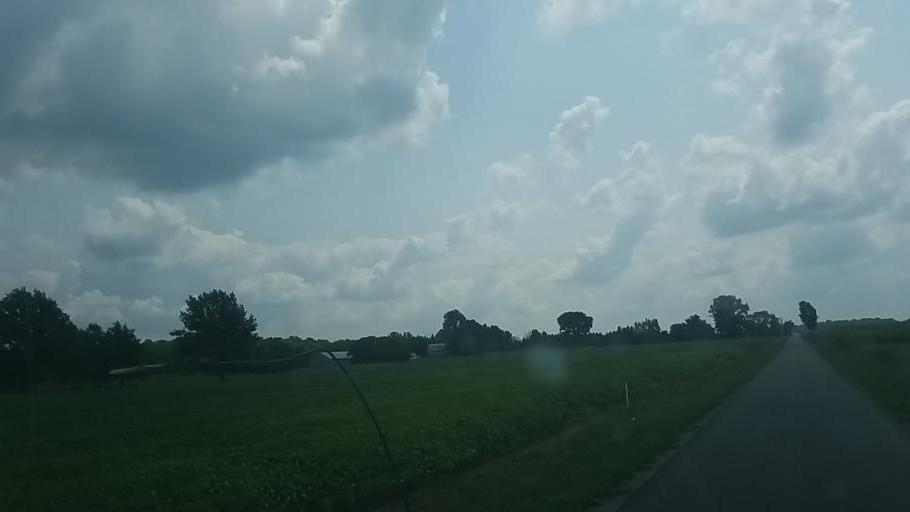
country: US
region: Ohio
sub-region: Wyandot County
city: Carey
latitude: 40.9747
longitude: -83.2855
